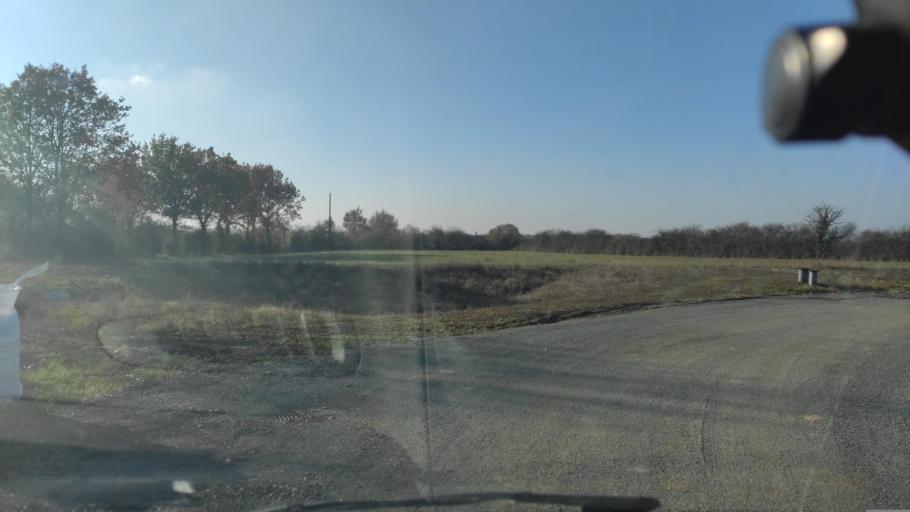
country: FR
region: Pays de la Loire
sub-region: Departement de la Vendee
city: Les Essarts
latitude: 46.7698
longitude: -1.2419
